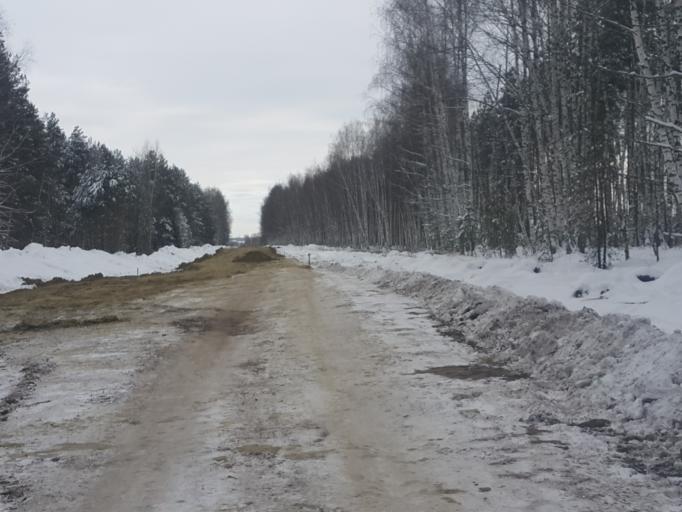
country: RU
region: Tambov
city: Platonovka
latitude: 52.8842
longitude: 41.8622
